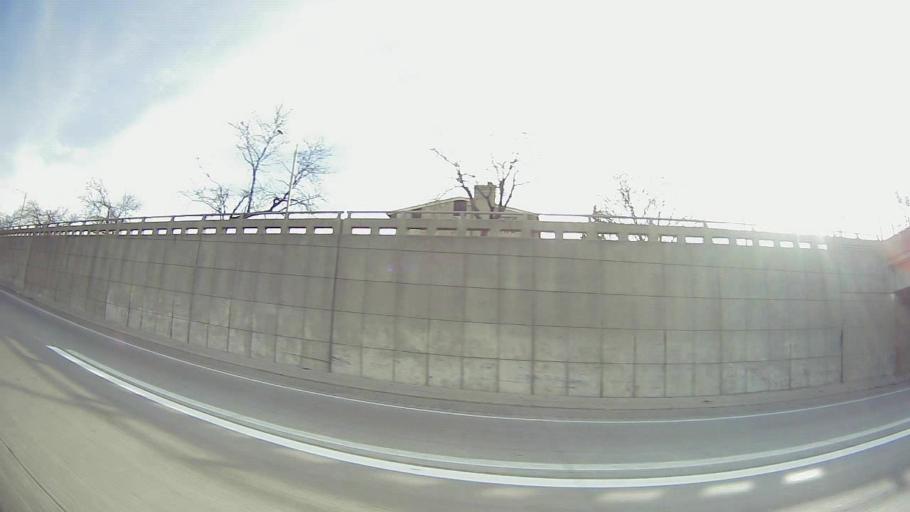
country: US
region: Michigan
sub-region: Wayne County
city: Redford
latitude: 42.3855
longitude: -83.2708
